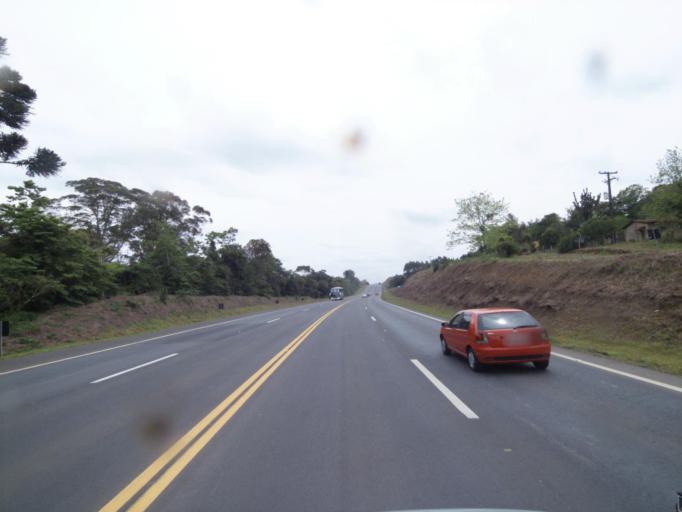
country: BR
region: Parana
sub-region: Irati
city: Irati
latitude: -25.4651
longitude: -50.5858
